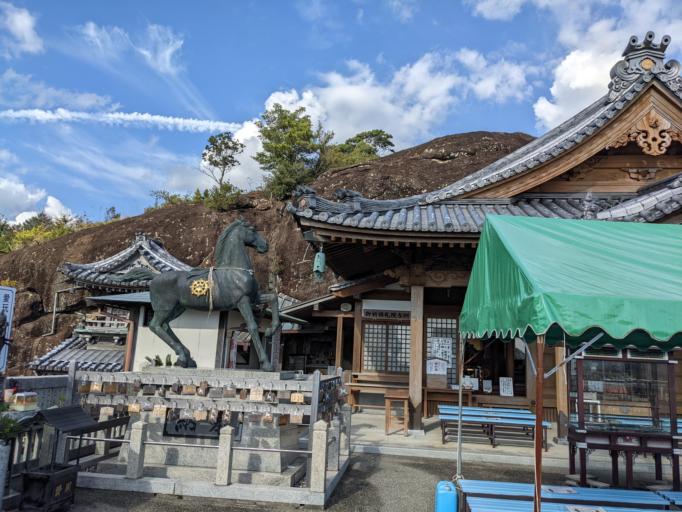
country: JP
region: Wakayama
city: Tanabe
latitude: 33.7138
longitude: 135.4279
